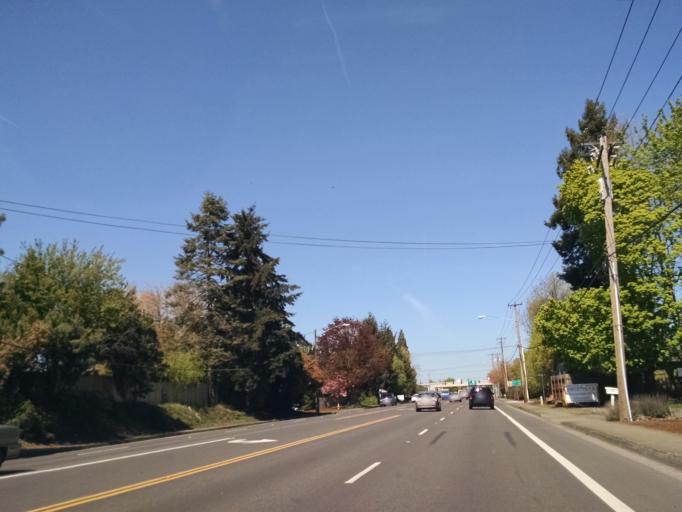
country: US
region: Oregon
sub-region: Lane County
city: Eugene
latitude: 44.0842
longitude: -123.0675
